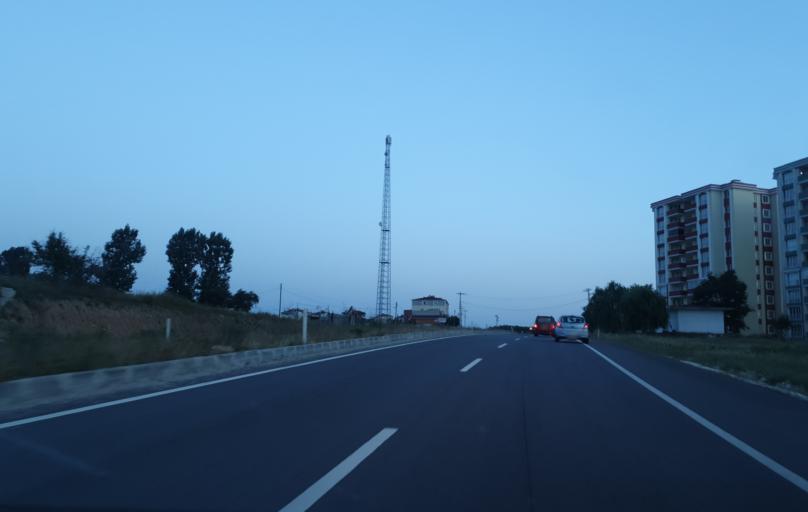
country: TR
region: Tekirdag
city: Saray
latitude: 41.3677
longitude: 27.9417
